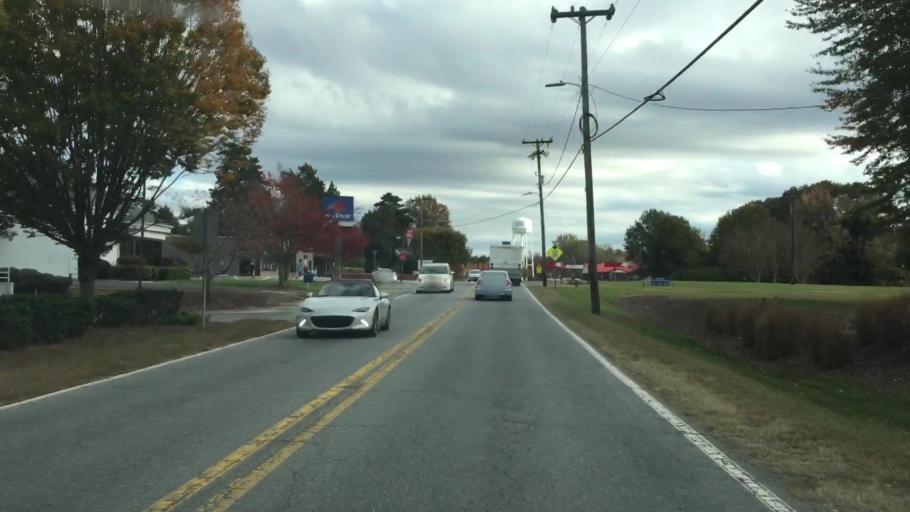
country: US
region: North Carolina
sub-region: Guilford County
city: Stokesdale
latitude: 36.2396
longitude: -79.9822
